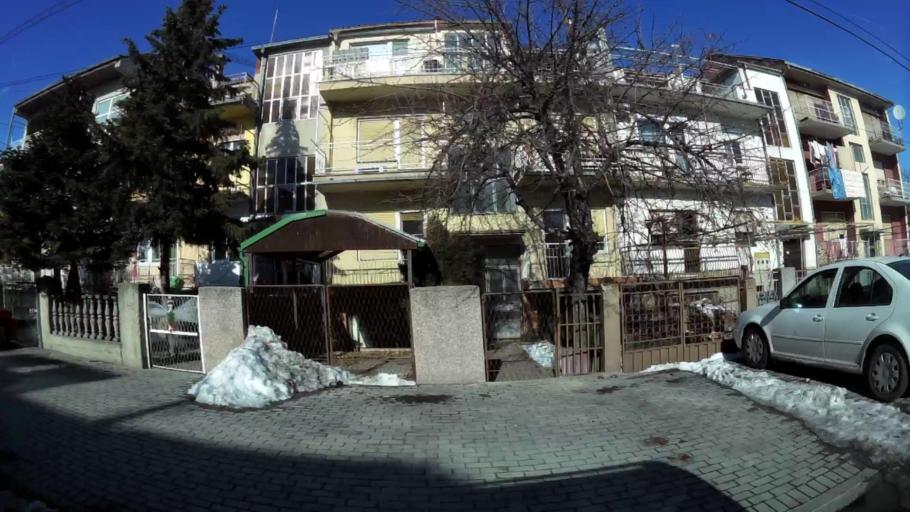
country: MK
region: Saraj
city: Saraj
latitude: 42.0047
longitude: 21.3512
